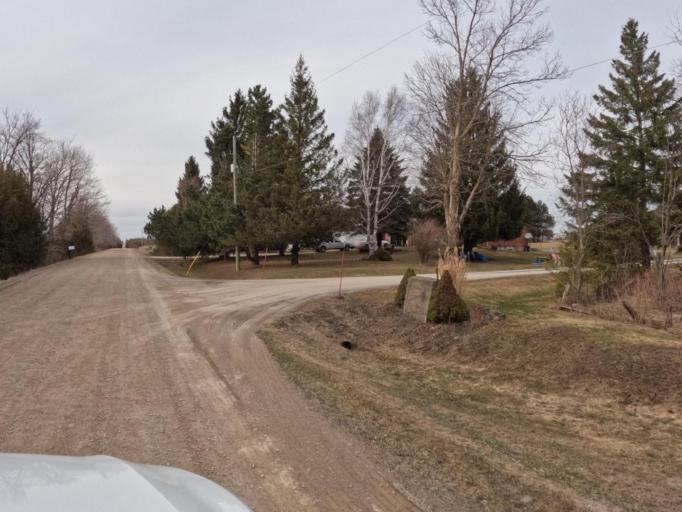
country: CA
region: Ontario
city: Shelburne
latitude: 43.9319
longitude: -80.2580
